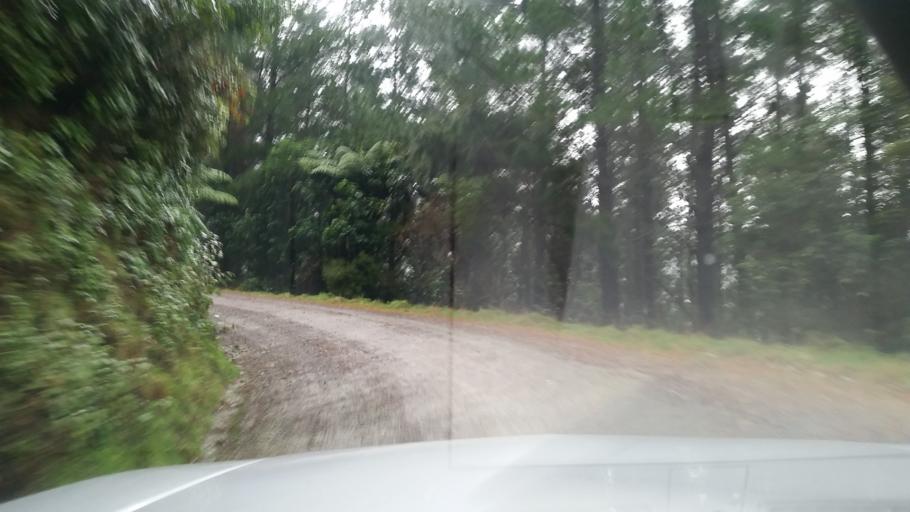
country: NZ
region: Marlborough
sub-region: Marlborough District
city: Picton
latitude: -41.1379
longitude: 174.0534
